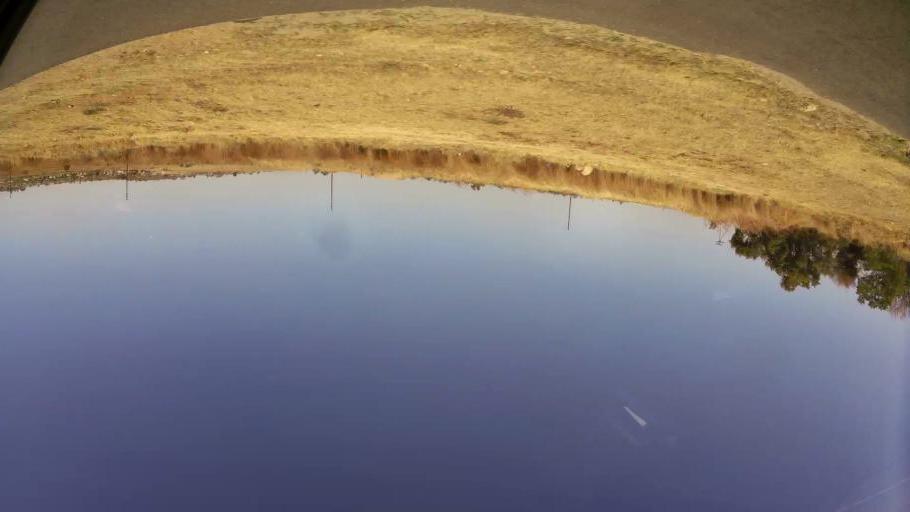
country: ZA
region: Gauteng
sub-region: City of Johannesburg Metropolitan Municipality
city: Diepsloot
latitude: -25.9791
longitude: 27.9322
